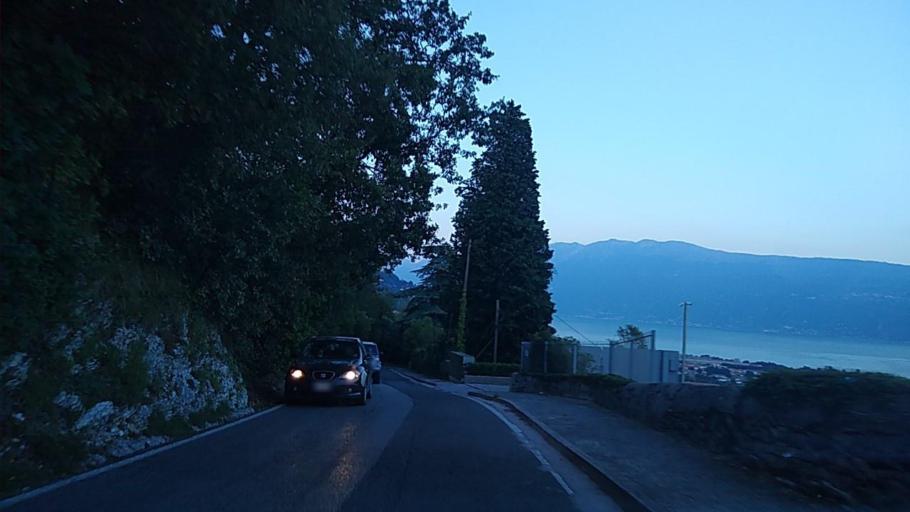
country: IT
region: Lombardy
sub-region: Provincia di Brescia
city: Toscolano Maderno
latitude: 45.6365
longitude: 10.5946
